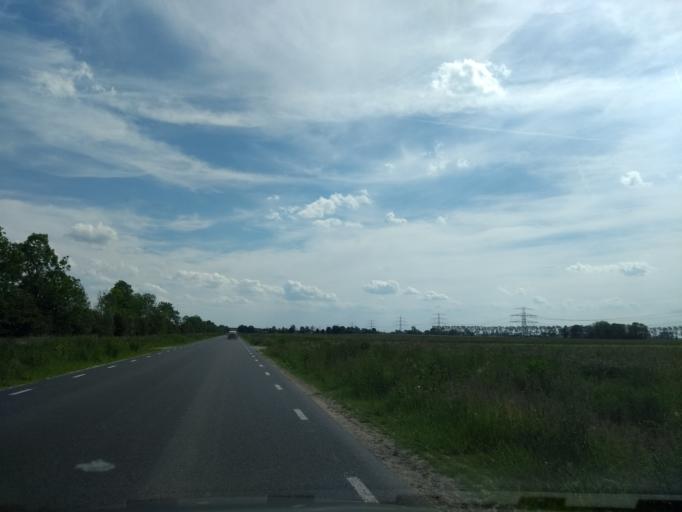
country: NL
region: Groningen
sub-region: Gemeente Zuidhorn
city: Aduard
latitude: 53.2566
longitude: 6.4813
